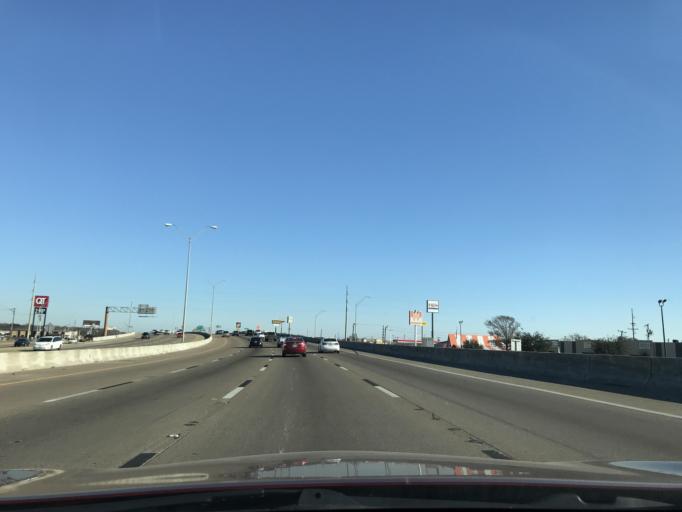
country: US
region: Texas
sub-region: Tarrant County
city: Forest Hill
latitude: 32.6617
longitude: -97.2847
